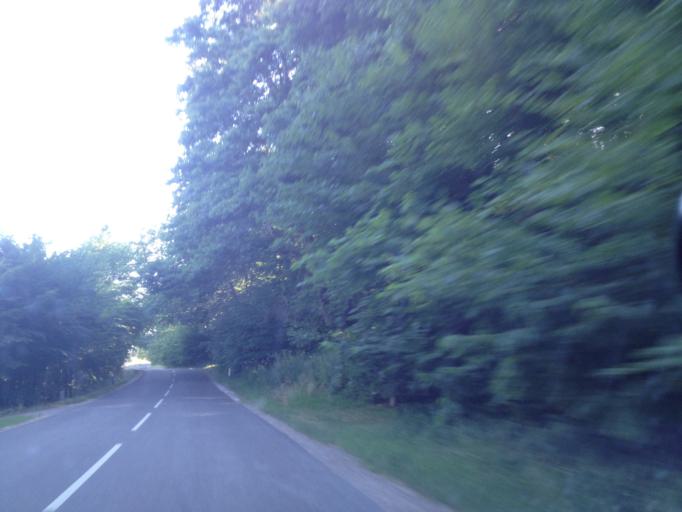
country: DK
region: Capital Region
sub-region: Gribskov Kommune
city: Helsinge
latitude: 56.0404
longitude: 12.1078
